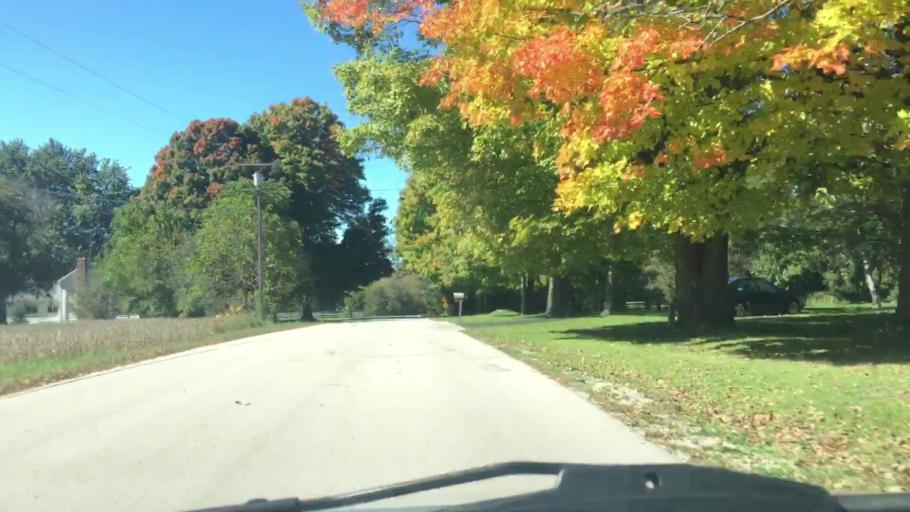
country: US
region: Wisconsin
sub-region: Waukesha County
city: North Prairie
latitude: 42.9303
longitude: -88.4496
